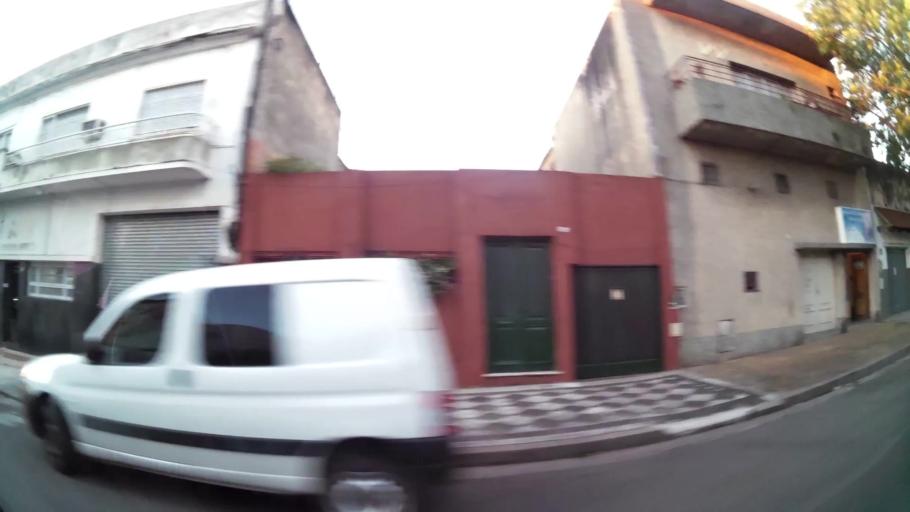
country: AR
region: Buenos Aires F.D.
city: Buenos Aires
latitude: -34.6390
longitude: -58.4296
